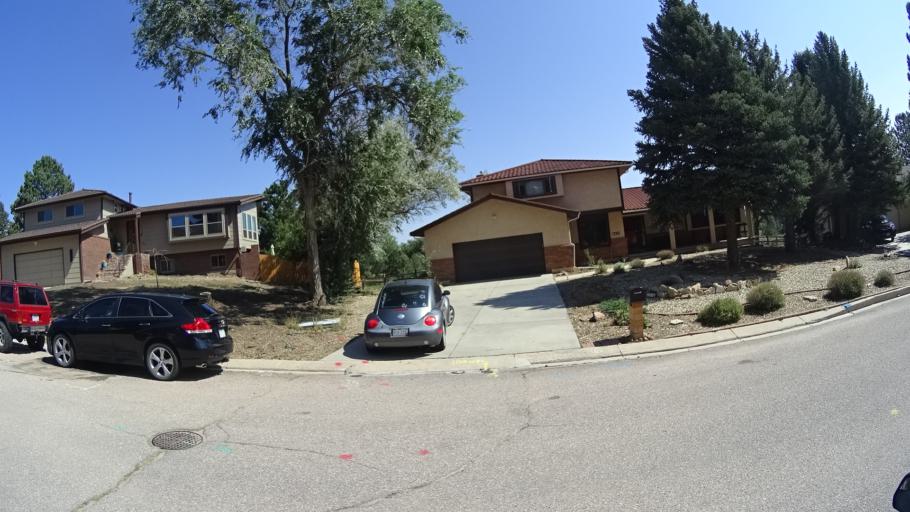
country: US
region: Colorado
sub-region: El Paso County
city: Air Force Academy
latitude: 38.9247
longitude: -104.8243
